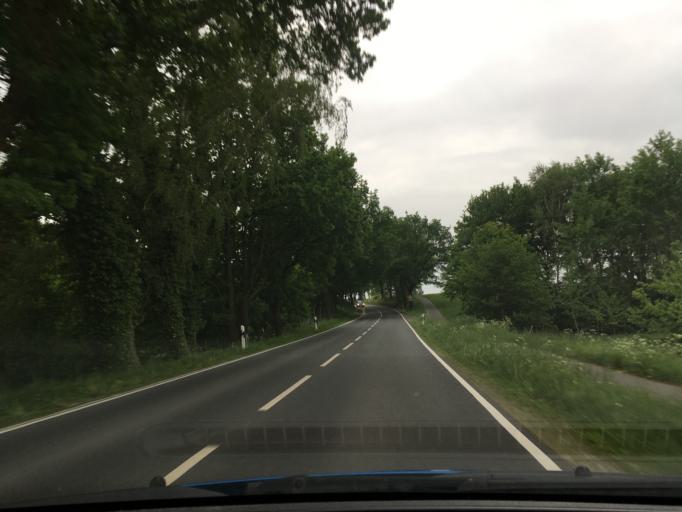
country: DE
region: Lower Saxony
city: Wulfsen
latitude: 53.3373
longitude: 10.1478
